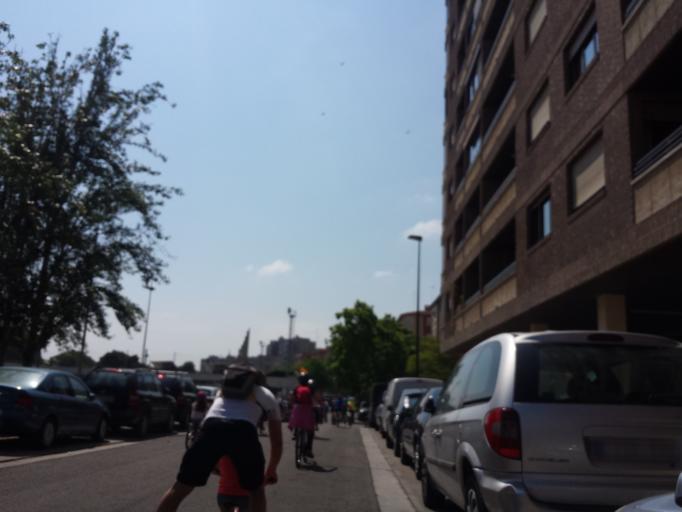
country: ES
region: Aragon
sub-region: Provincia de Zaragoza
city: Almozara
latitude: 41.6623
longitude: -0.8955
